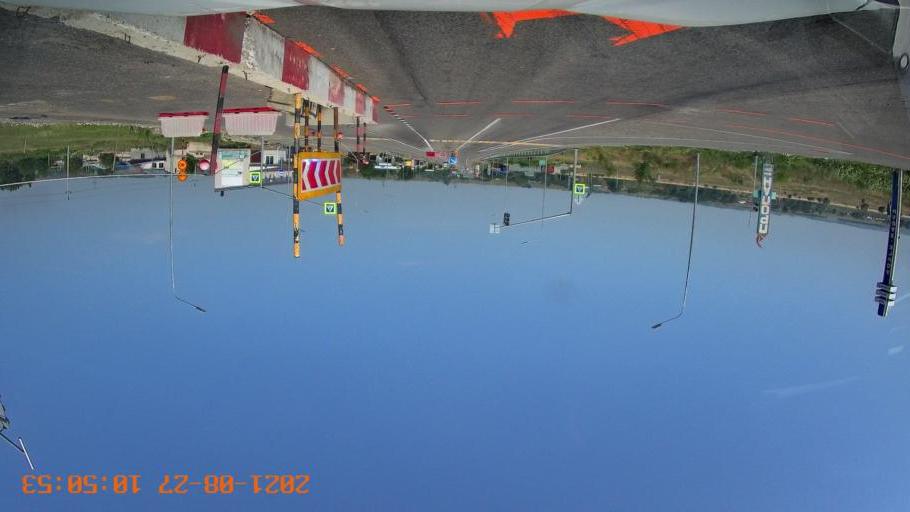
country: RU
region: Karachayevo-Cherkesiya
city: Adyge-Khabl'
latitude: 44.3607
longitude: 41.9426
